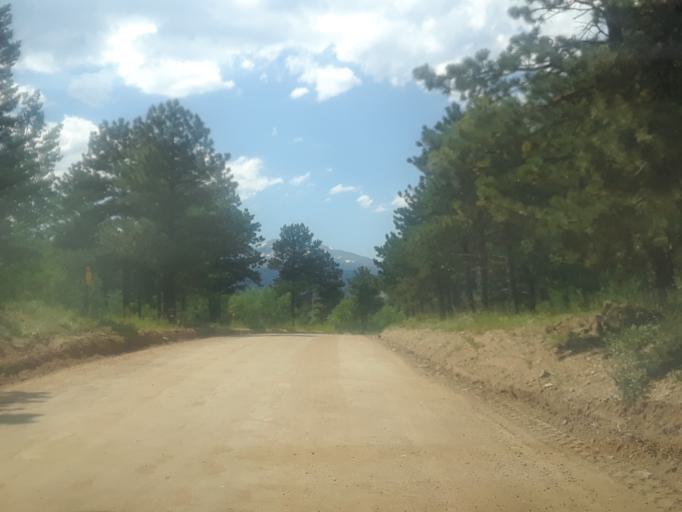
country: US
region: Colorado
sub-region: Boulder County
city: Nederland
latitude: 40.0586
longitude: -105.4298
